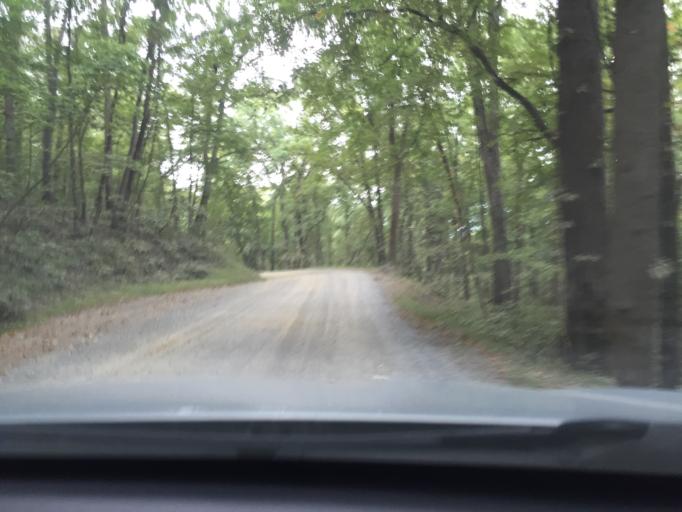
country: US
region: Virginia
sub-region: Shenandoah County
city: Woodstock
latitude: 38.8708
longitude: -78.4542
